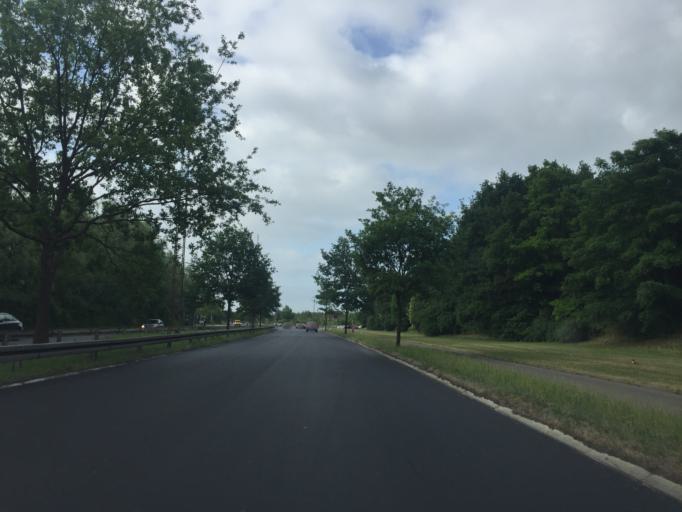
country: DK
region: Capital Region
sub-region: Hvidovre Kommune
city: Hvidovre
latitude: 55.6600
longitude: 12.4542
